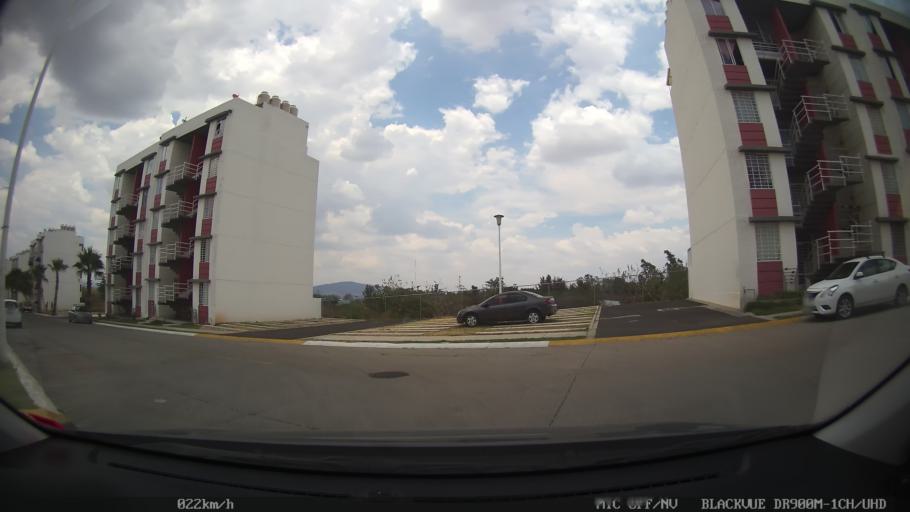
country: MX
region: Jalisco
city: Tonala
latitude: 20.6387
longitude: -103.2248
